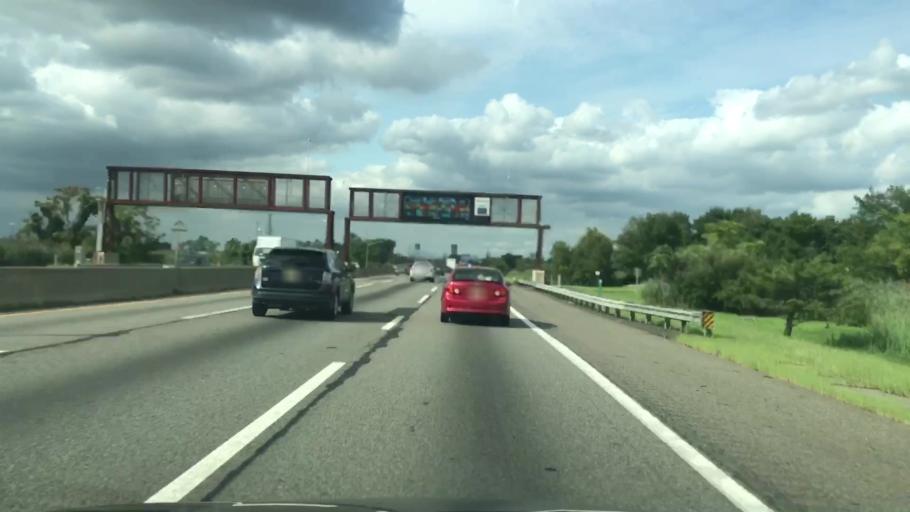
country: US
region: New Jersey
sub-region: Hudson County
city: North Bergen
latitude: 40.8179
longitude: -74.0275
